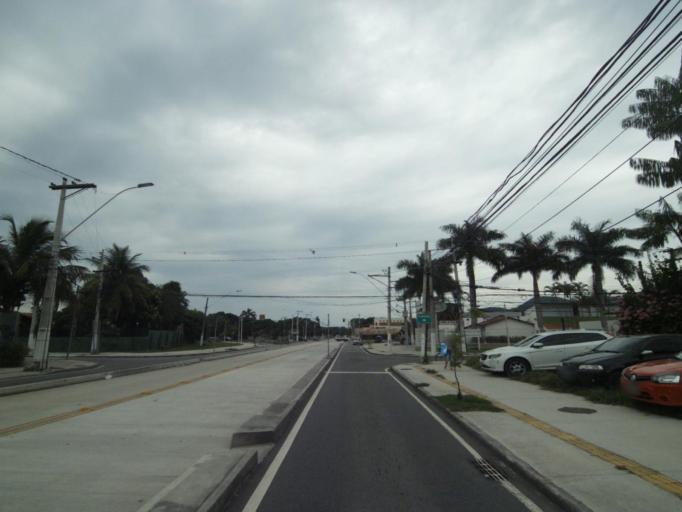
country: BR
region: Rio de Janeiro
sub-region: Niteroi
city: Niteroi
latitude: -22.9338
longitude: -43.0692
